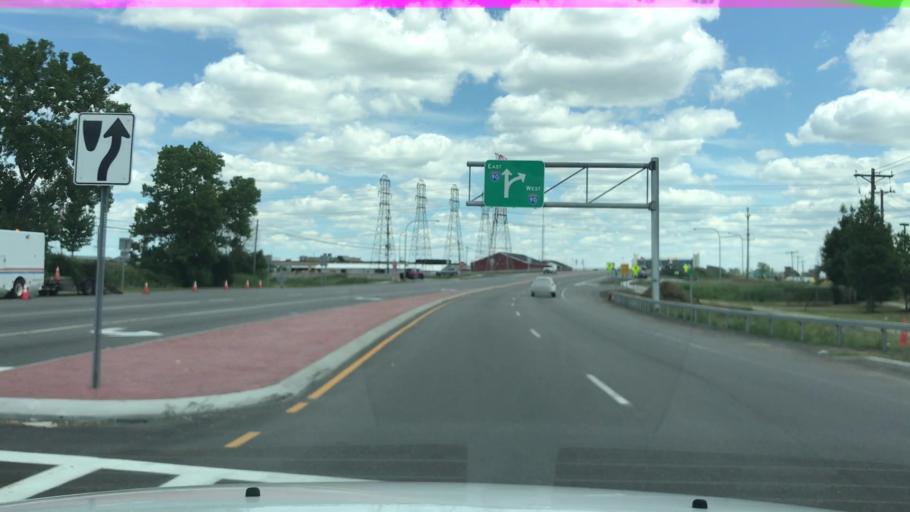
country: US
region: New York
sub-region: Erie County
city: Cheektowaga
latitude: 42.9088
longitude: -78.7713
